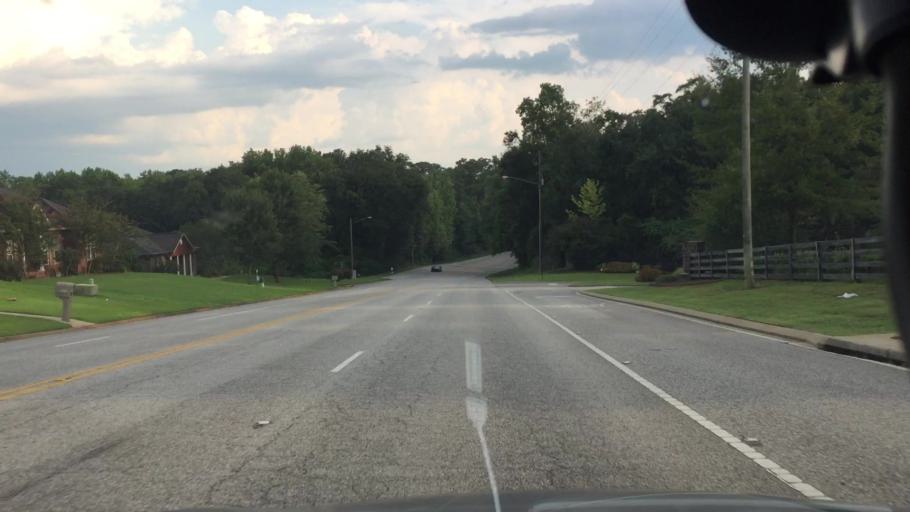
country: US
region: Alabama
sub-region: Coffee County
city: Enterprise
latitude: 31.3563
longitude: -85.8327
